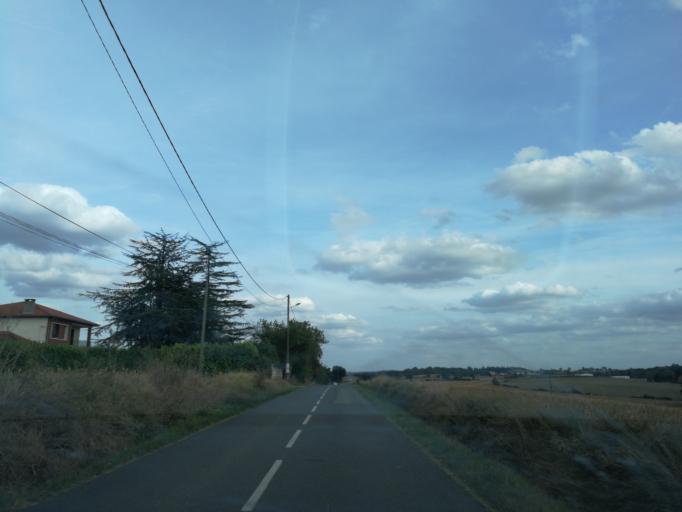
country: FR
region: Midi-Pyrenees
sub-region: Departement de la Haute-Garonne
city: Flourens
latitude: 43.6107
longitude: 1.5341
